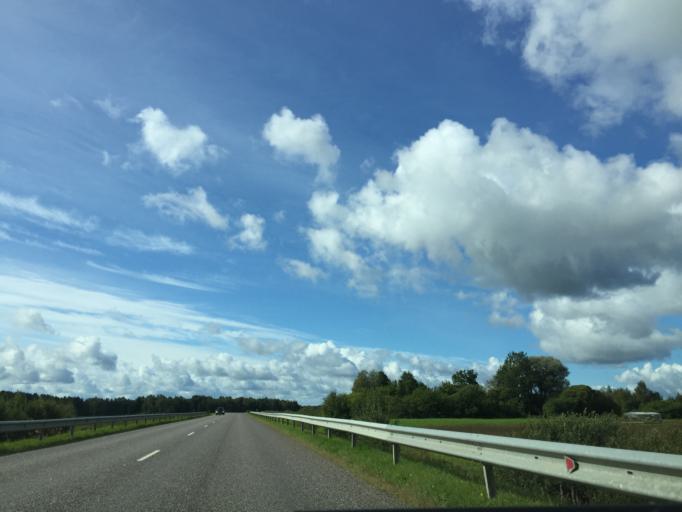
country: LV
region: Kuldigas Rajons
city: Kuldiga
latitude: 56.9999
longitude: 22.1318
